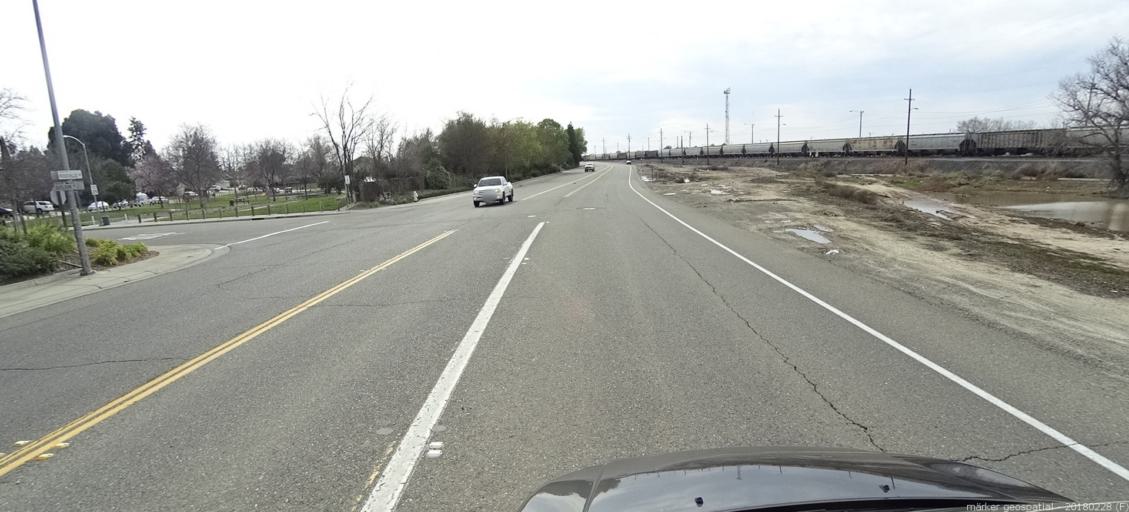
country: US
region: California
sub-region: Sacramento County
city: Antelope
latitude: 38.7159
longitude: -121.3180
